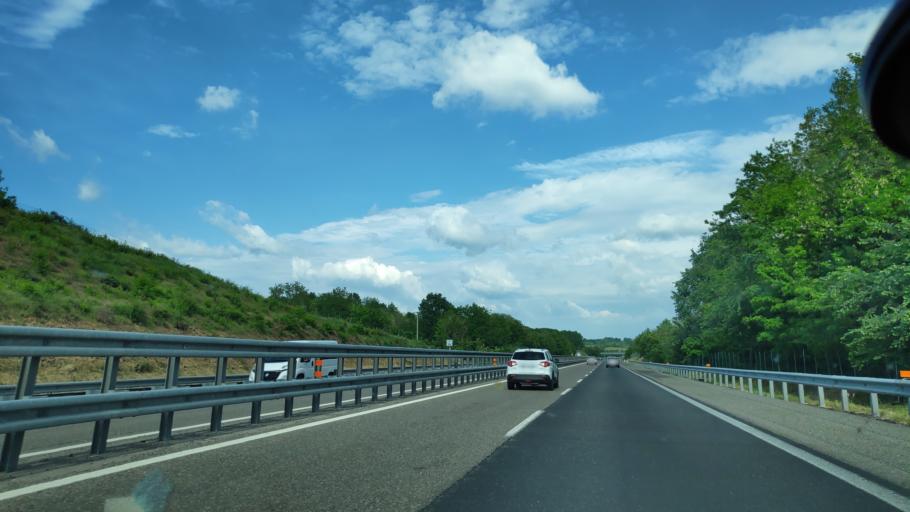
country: IT
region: Piedmont
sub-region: Provincia di Asti
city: Tigliole
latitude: 44.9019
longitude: 8.0696
